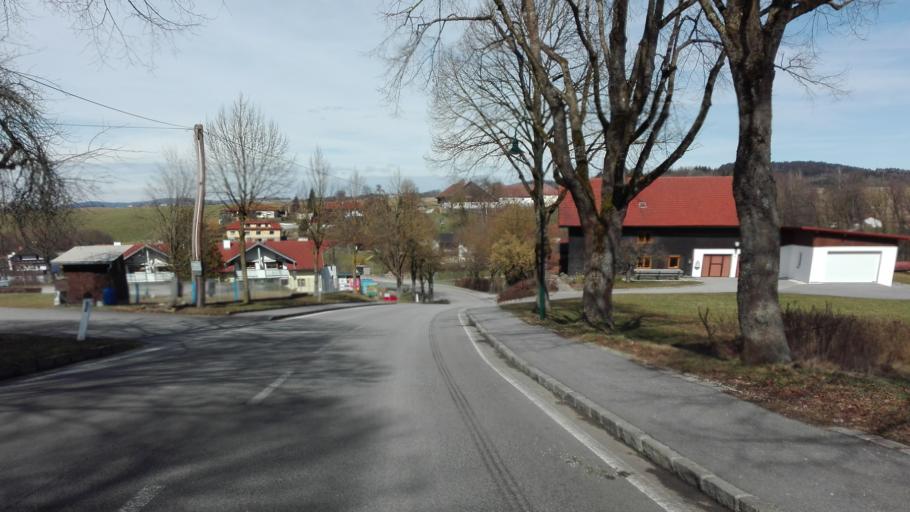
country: DE
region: Bavaria
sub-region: Lower Bavaria
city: Obernzell
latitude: 48.3584
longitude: 13.6473
